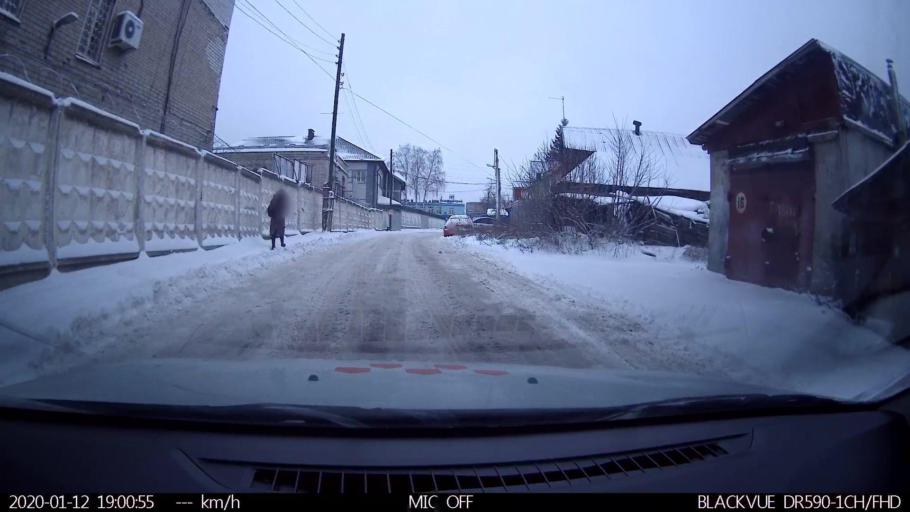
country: RU
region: Nizjnij Novgorod
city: Nizhniy Novgorod
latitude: 56.3308
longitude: 43.9100
